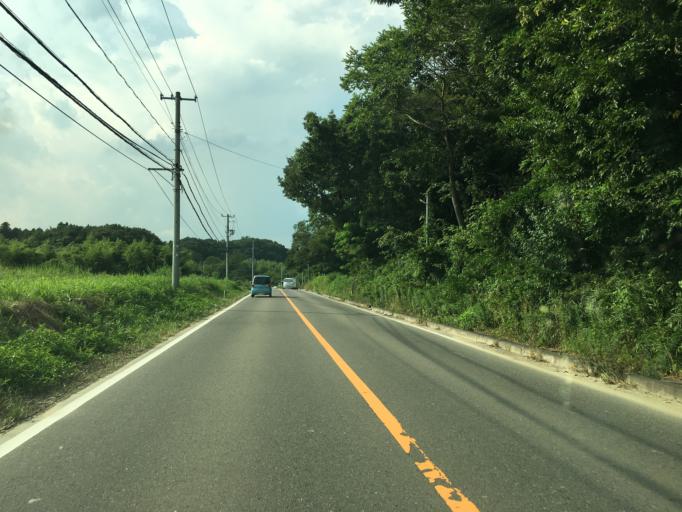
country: JP
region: Fukushima
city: Motomiya
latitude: 37.4659
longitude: 140.4247
